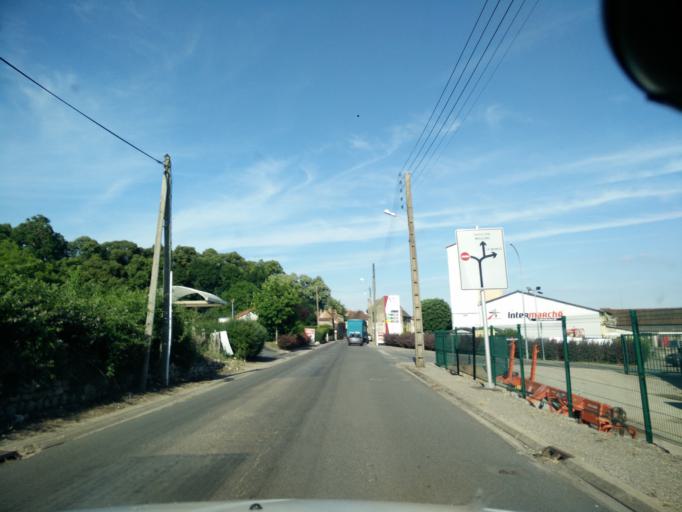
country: FR
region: Auvergne
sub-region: Departement de l'Allier
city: Souvigny
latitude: 46.5327
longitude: 3.1874
